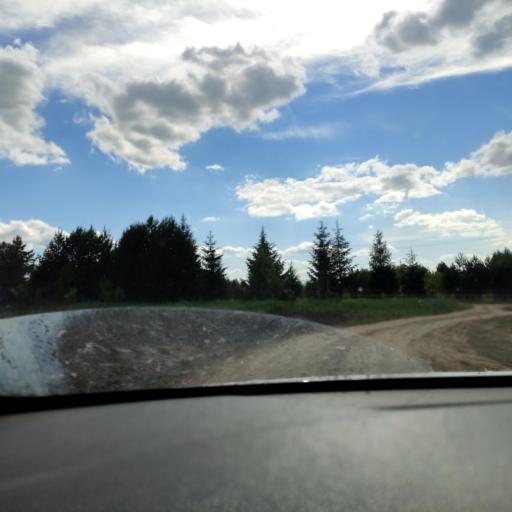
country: RU
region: Tatarstan
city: Vysokaya Gora
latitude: 56.1910
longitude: 49.2059
